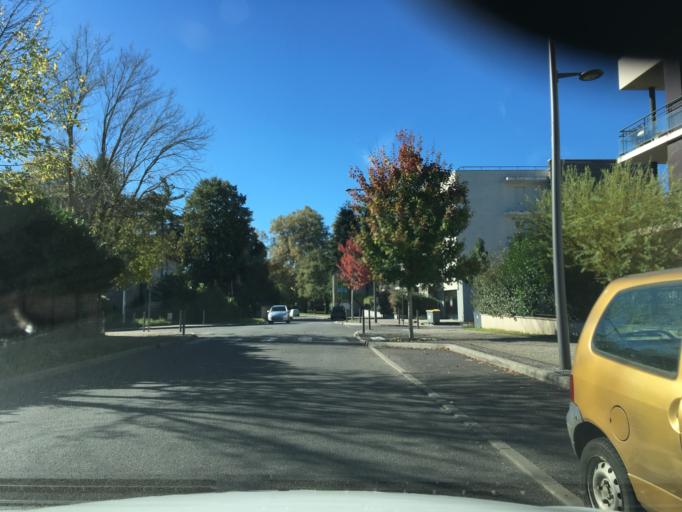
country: FR
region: Aquitaine
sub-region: Departement des Pyrenees-Atlantiques
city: Pau
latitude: 43.3153
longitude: -0.3489
